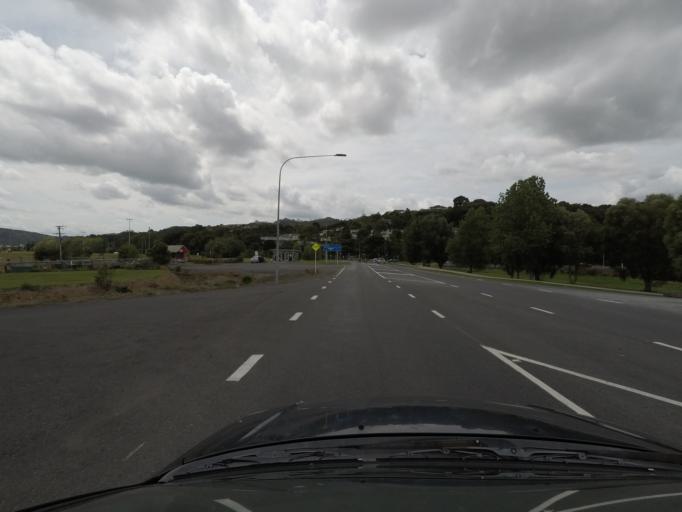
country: NZ
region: Northland
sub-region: Whangarei
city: Whangarei
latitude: -35.7328
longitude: 174.3429
